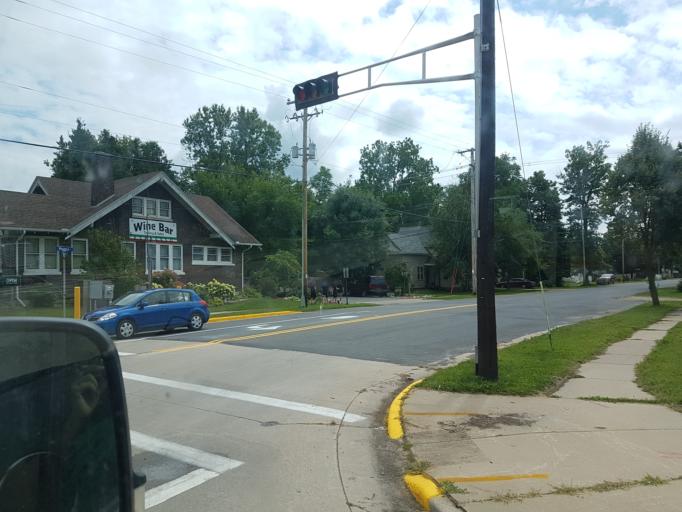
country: US
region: Wisconsin
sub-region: Waushara County
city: Wautoma
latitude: 44.0759
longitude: -89.2938
